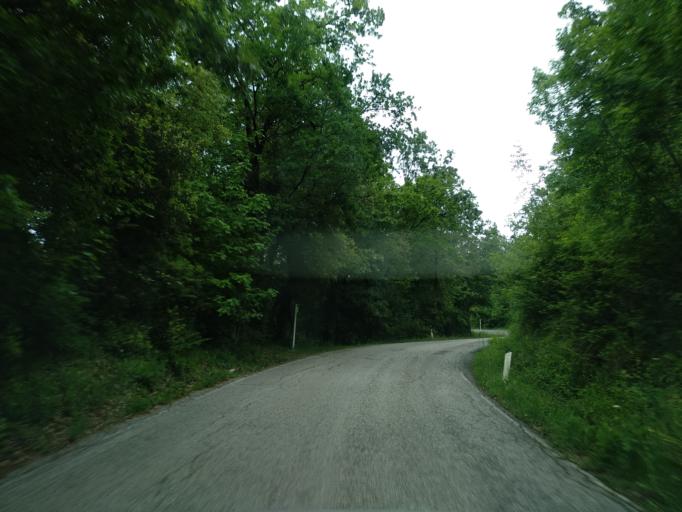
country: IT
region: Tuscany
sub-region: Provincia di Livorno
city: Guasticce
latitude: 43.5674
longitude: 10.4213
